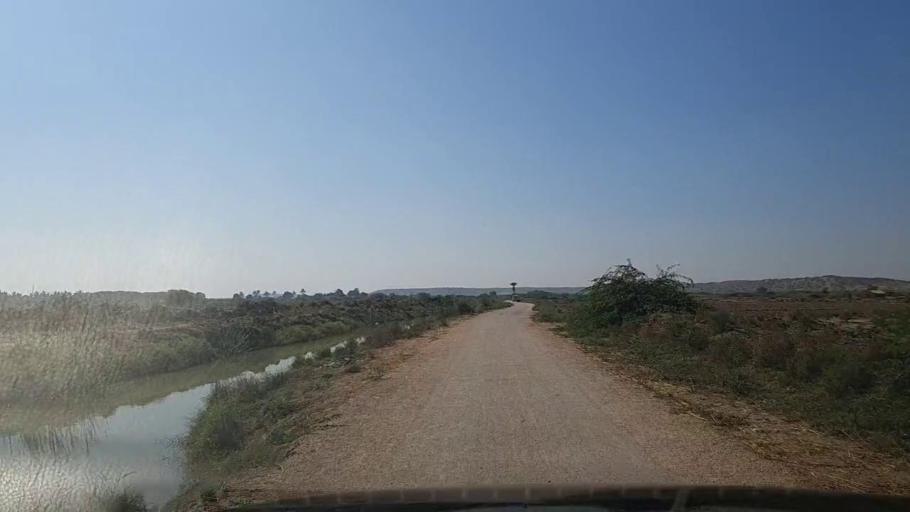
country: PK
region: Sindh
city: Thatta
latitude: 24.6321
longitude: 67.8717
